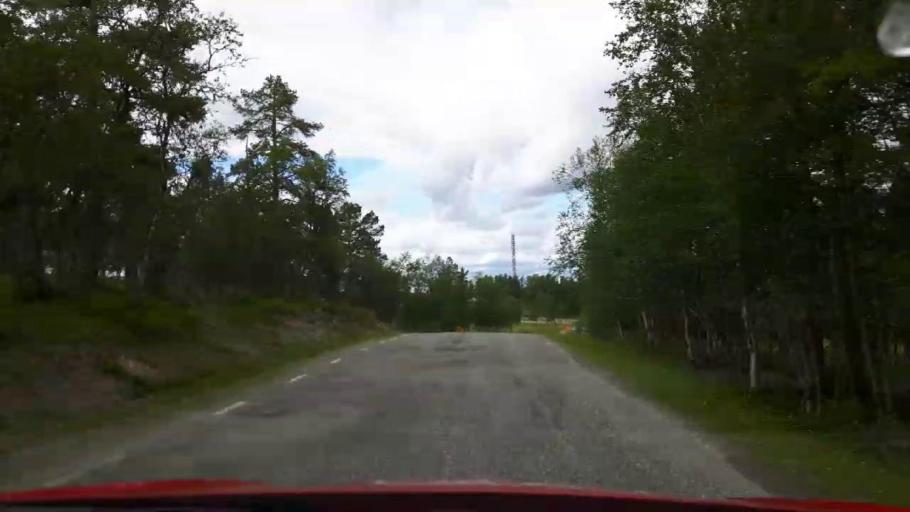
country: NO
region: Hedmark
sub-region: Engerdal
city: Engerdal
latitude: 62.2863
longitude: 12.8362
